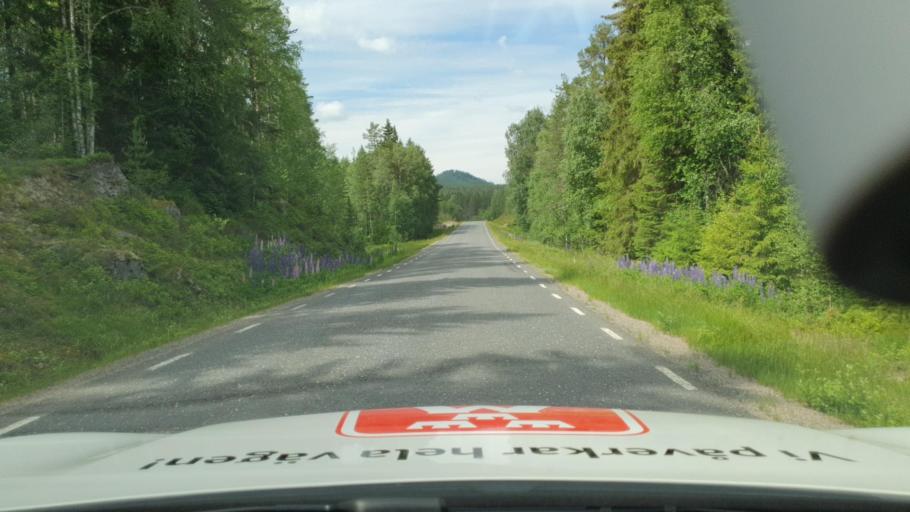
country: SE
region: Vaermland
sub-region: Torsby Kommun
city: Torsby
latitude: 60.6725
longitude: 12.6897
